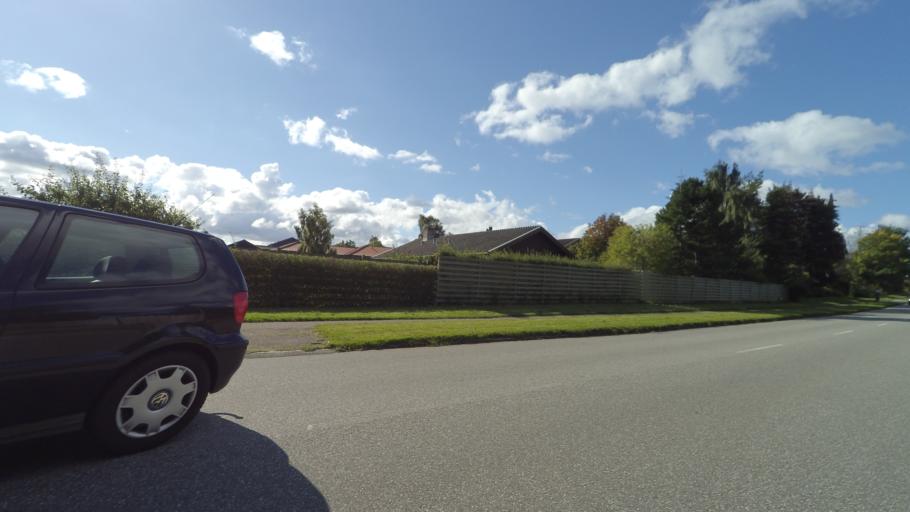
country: DK
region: Central Jutland
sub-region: Arhus Kommune
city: Arhus
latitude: 56.1142
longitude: 10.1863
